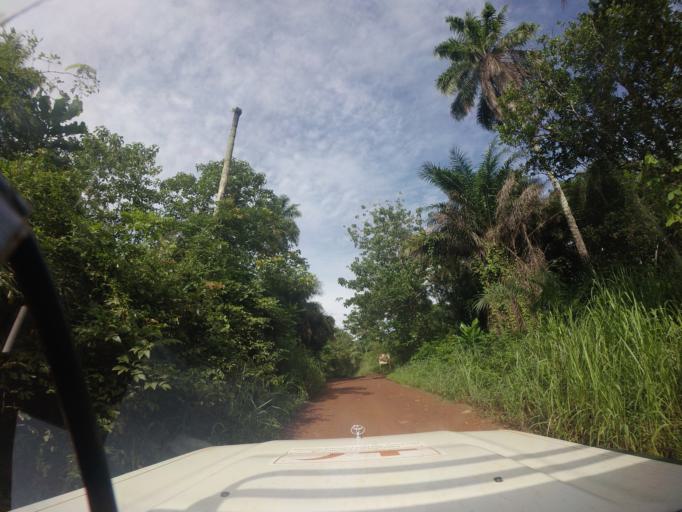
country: SL
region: Northern Province
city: Kambia
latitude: 9.1173
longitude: -12.9433
